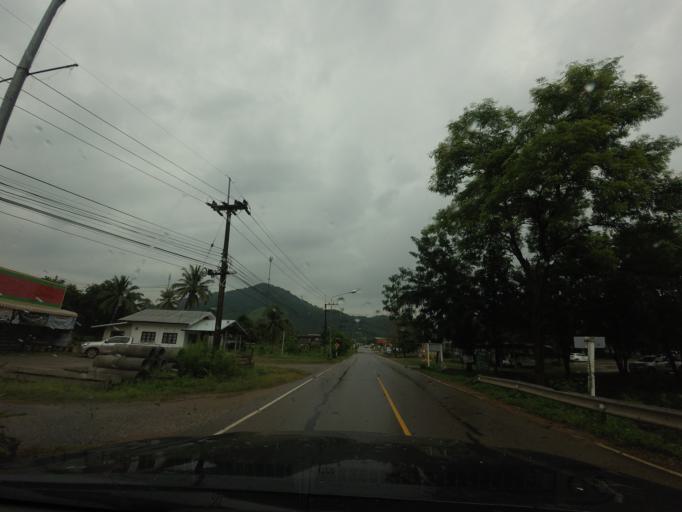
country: TH
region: Nong Khai
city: Sangkhom
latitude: 18.1729
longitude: 102.1694
